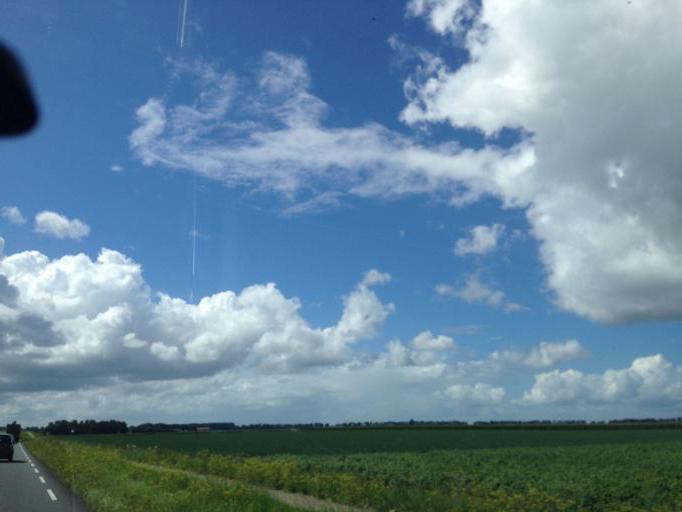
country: NL
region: Flevoland
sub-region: Gemeente Dronten
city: Dronten
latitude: 52.5399
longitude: 5.7813
